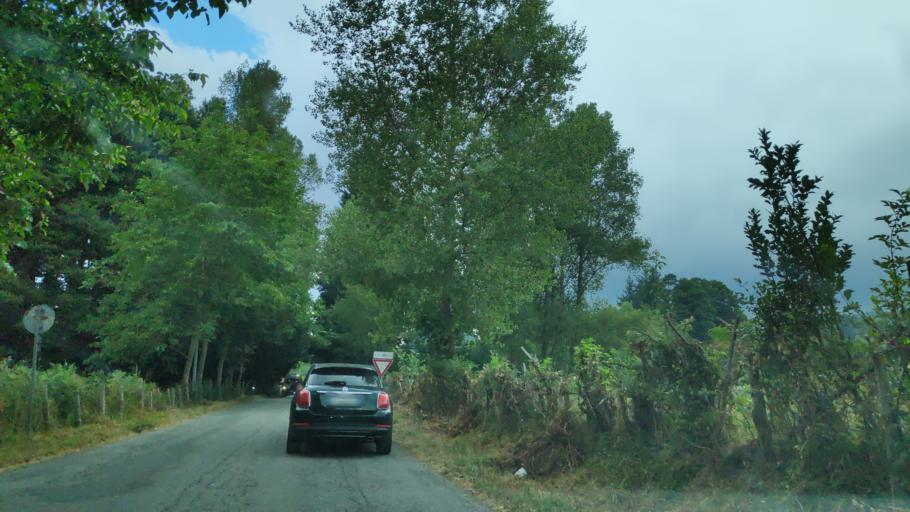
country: IT
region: Calabria
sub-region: Provincia di Vibo-Valentia
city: Mongiana
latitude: 38.5312
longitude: 16.3213
